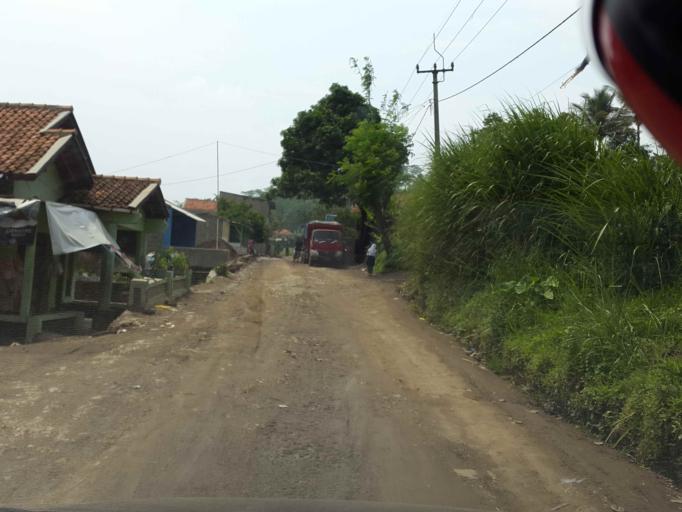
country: ID
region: West Java
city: Padalarang
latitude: -6.8565
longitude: 107.4552
